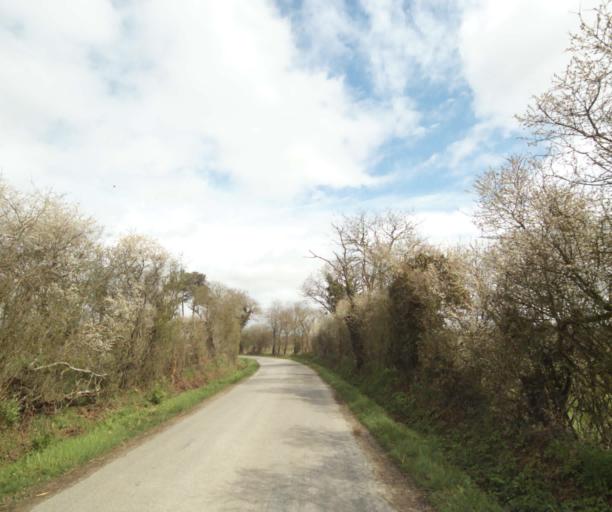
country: FR
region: Pays de la Loire
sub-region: Departement de la Loire-Atlantique
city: Bouvron
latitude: 47.4381
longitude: -1.8454
